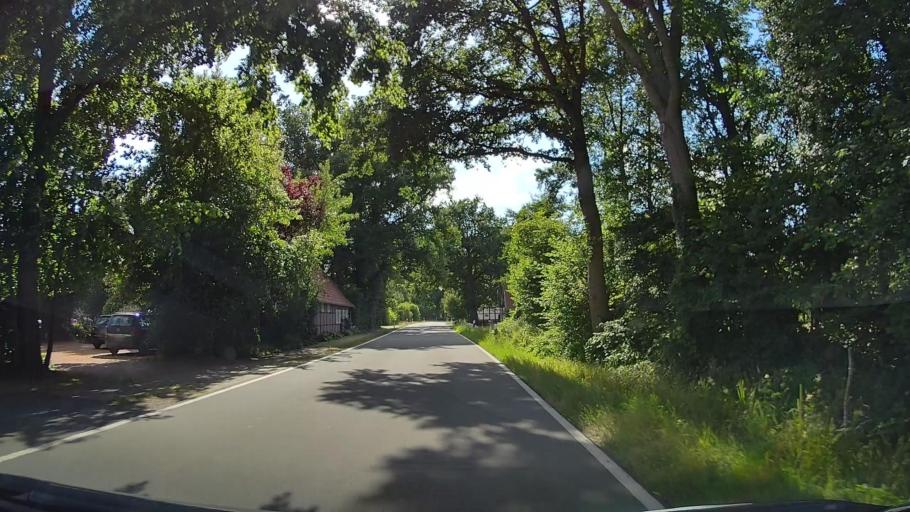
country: DE
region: Lower Saxony
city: Menslage
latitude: 52.6859
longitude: 7.7807
